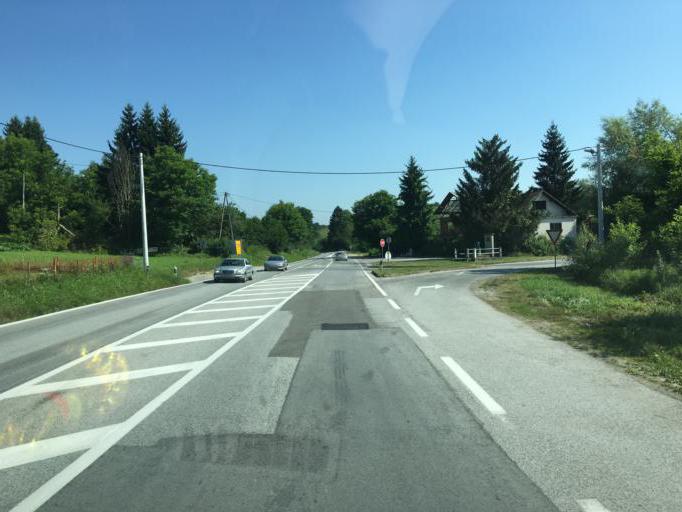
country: HR
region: Karlovacka
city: Vojnic
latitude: 45.3276
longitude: 15.6142
